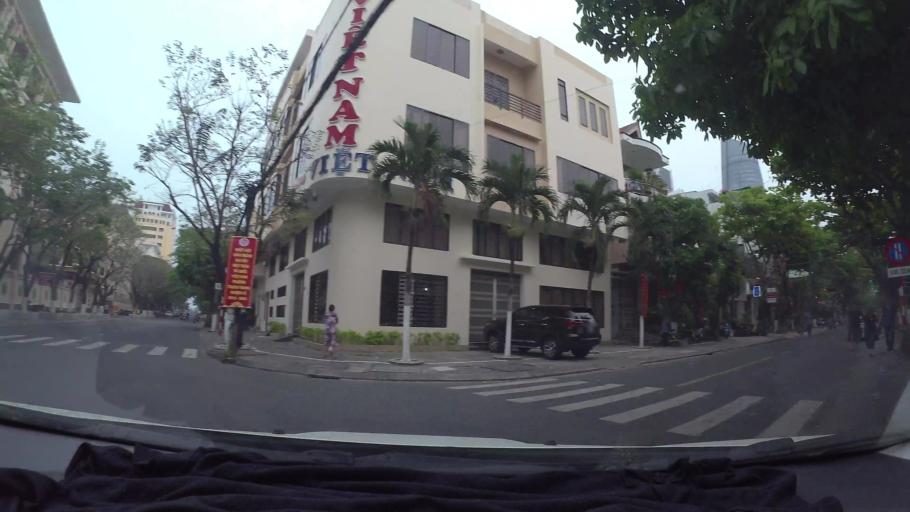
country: VN
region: Da Nang
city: Da Nang
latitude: 16.0803
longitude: 108.2213
